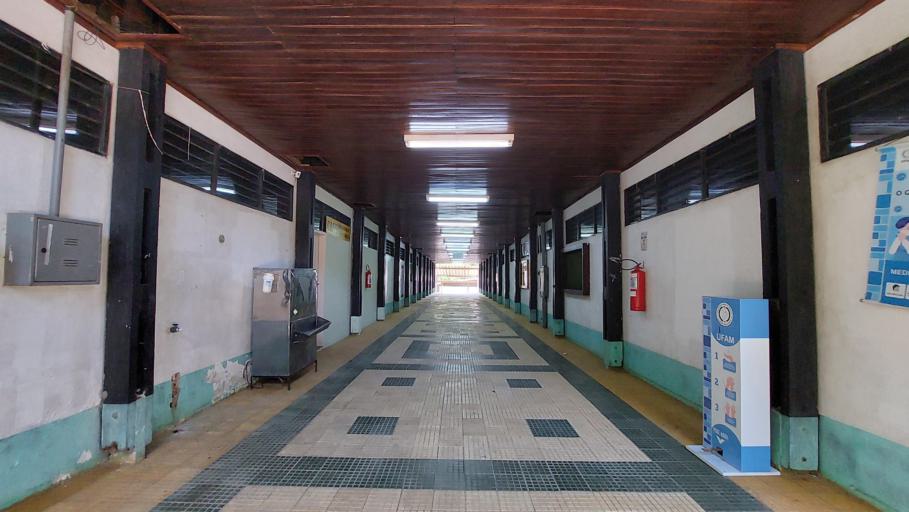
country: BR
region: Amazonas
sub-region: Manaus
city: Manaus
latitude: -3.1007
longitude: -59.9762
